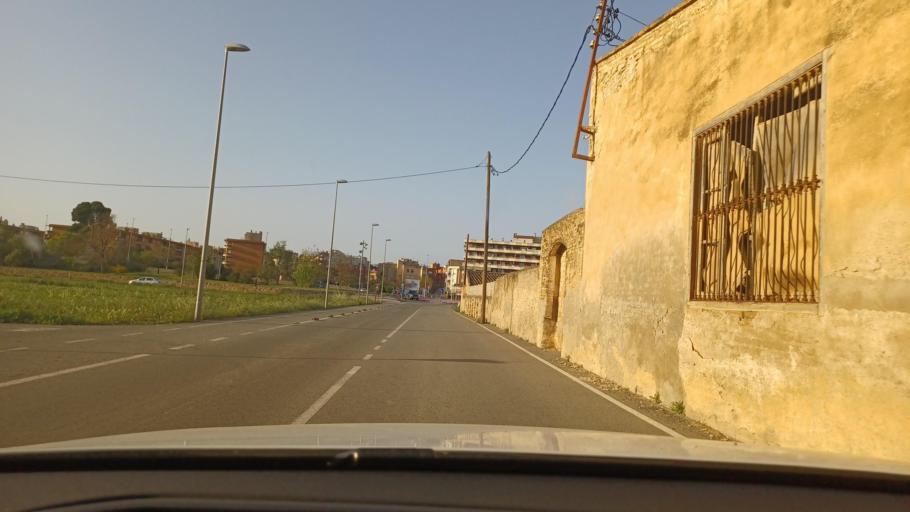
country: ES
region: Catalonia
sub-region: Provincia de Tarragona
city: Tortosa
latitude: 40.8010
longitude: 0.5184
